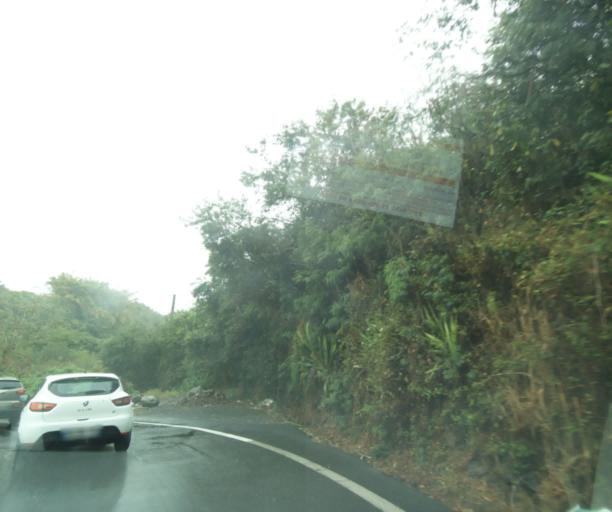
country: RE
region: Reunion
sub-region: Reunion
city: Saint-Paul
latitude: -21.0359
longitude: 55.2800
